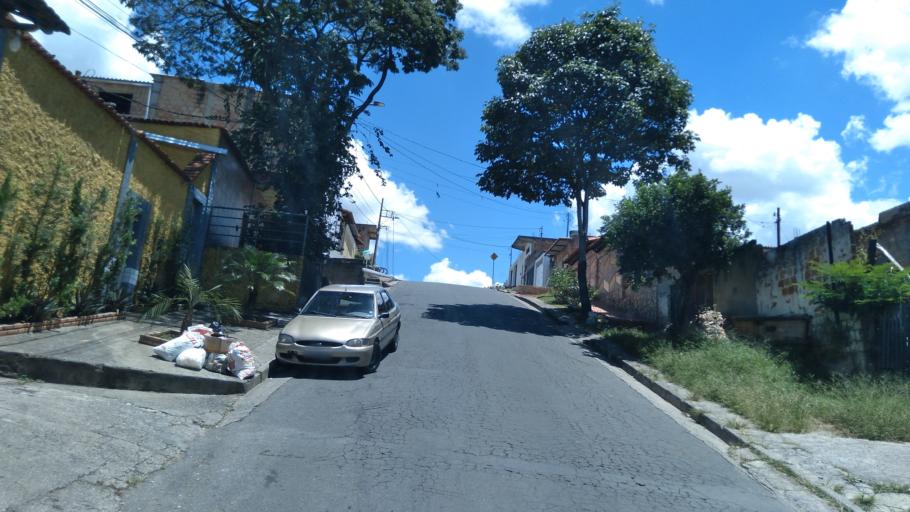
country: BR
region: Minas Gerais
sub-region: Santa Luzia
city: Santa Luzia
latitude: -19.8329
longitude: -43.8911
